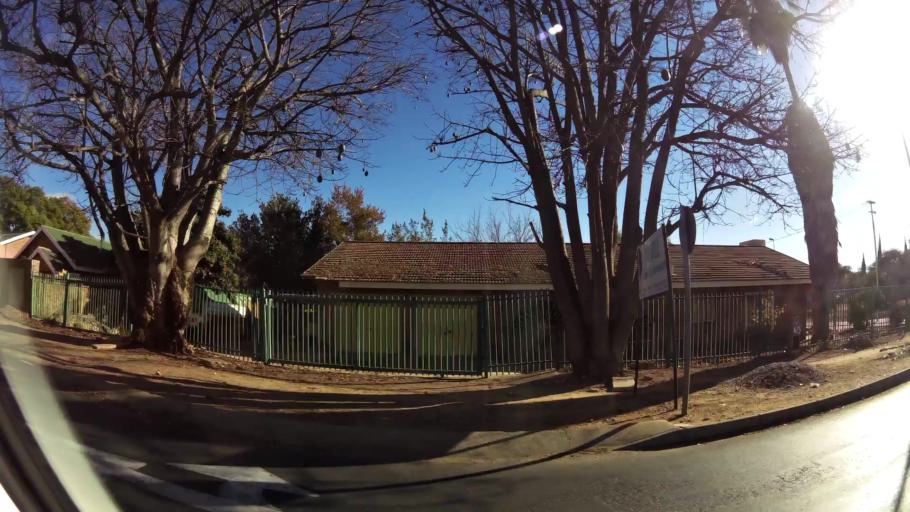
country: ZA
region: Limpopo
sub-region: Capricorn District Municipality
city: Polokwane
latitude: -23.9206
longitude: 29.4529
